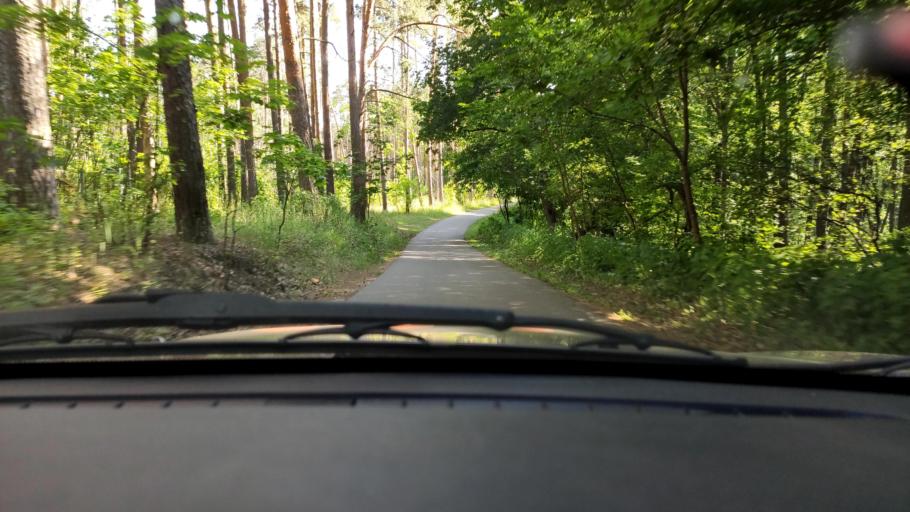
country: RU
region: Voronezj
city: Somovo
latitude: 51.8080
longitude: 39.3831
